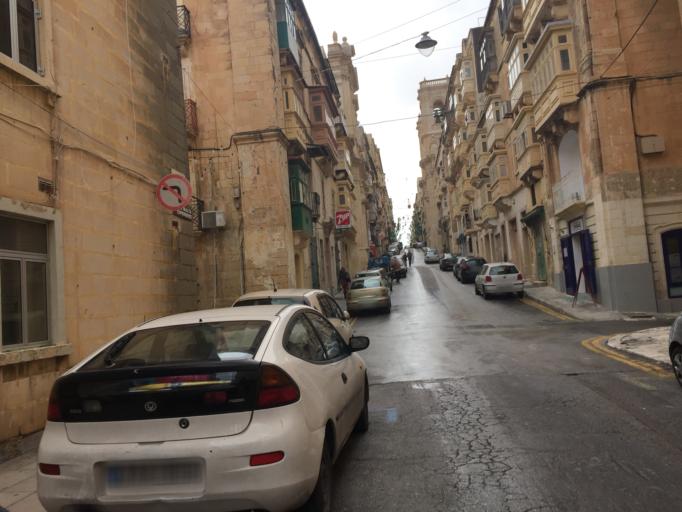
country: MT
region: Il-Belt Valletta
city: Valletta
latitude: 35.9000
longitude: 14.5172
